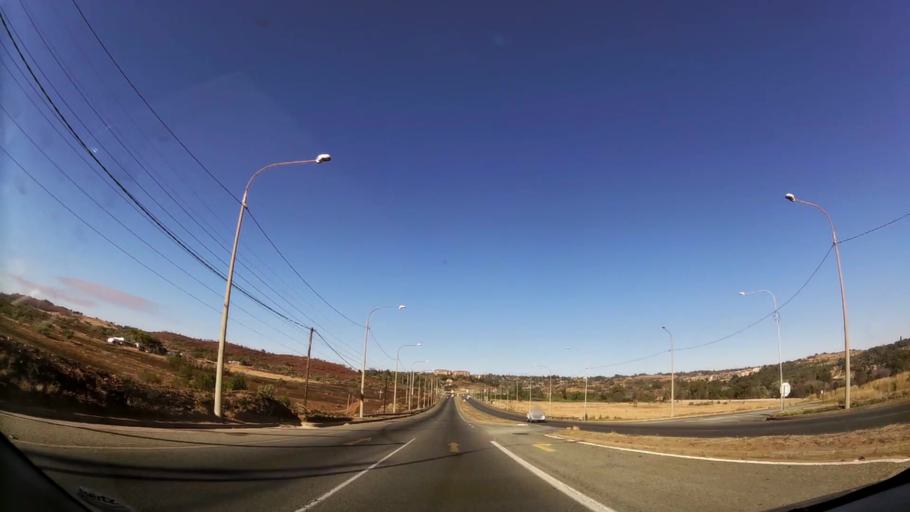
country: ZA
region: Gauteng
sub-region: West Rand District Municipality
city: Krugersdorp
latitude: -26.0677
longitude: 27.8038
